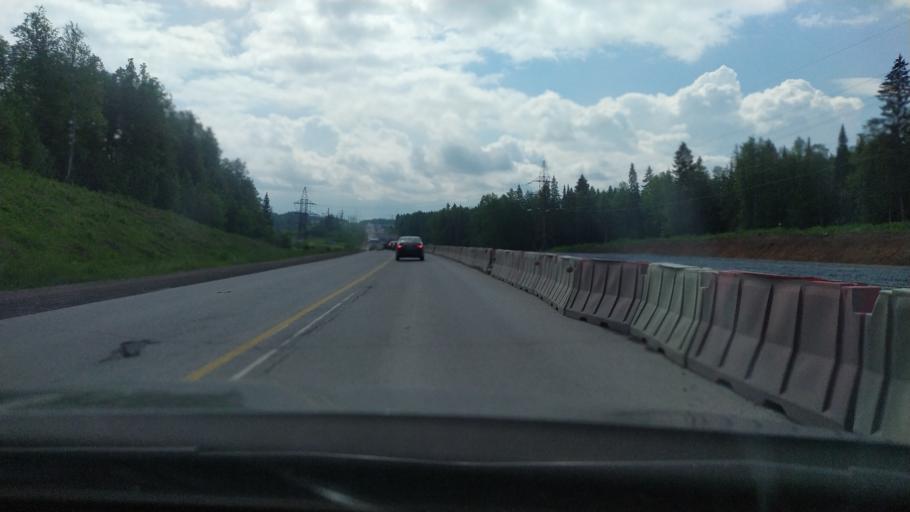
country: RU
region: Perm
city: Novyye Lyady
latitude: 58.0609
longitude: 56.4271
